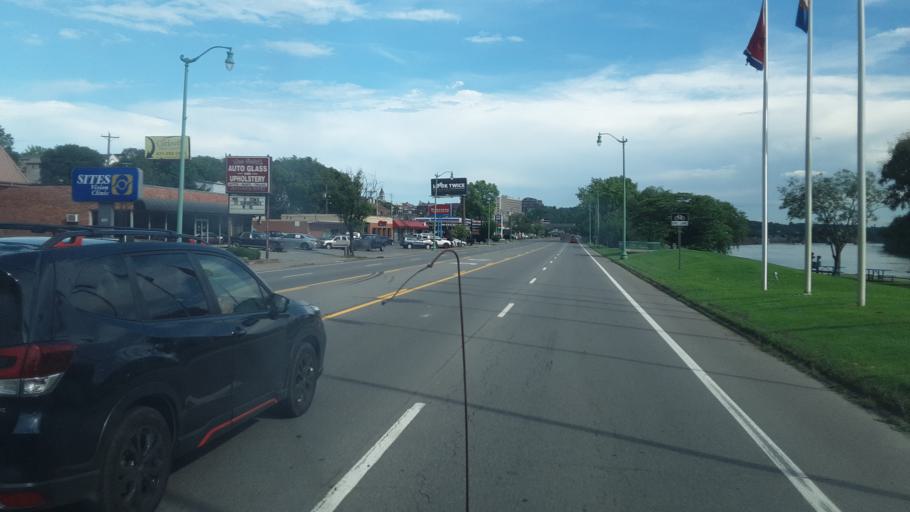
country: US
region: Tennessee
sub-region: Montgomery County
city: Clarksville
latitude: 36.5351
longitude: -87.3672
